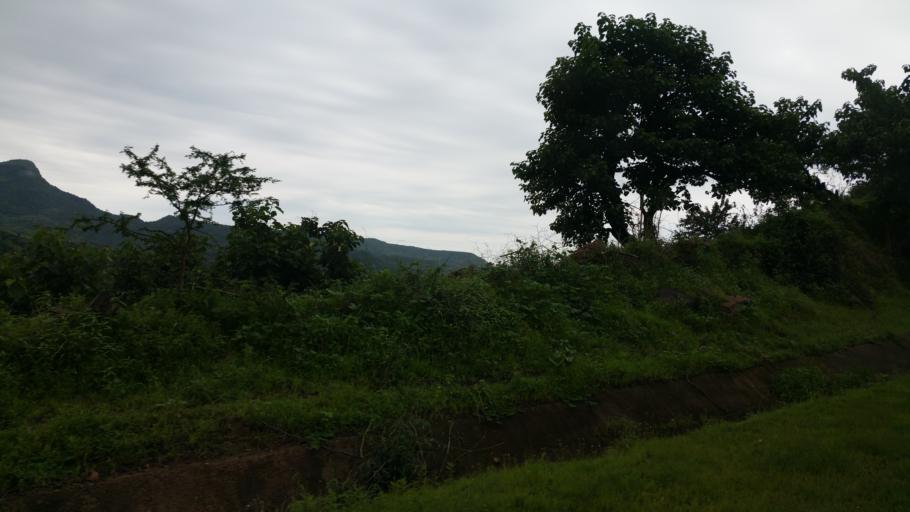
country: ET
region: Amhara
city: Debark'
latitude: 13.3818
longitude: 37.9856
